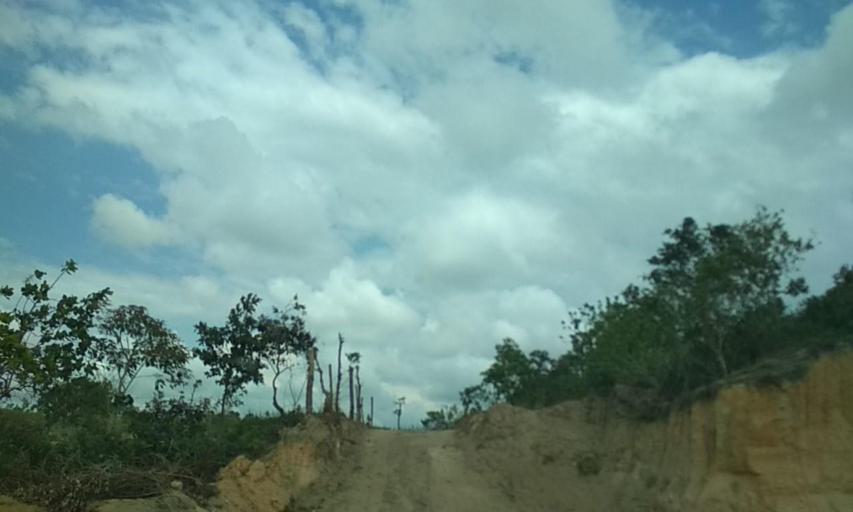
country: MX
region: Veracruz
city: Las Choapas
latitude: 17.9010
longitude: -94.1200
